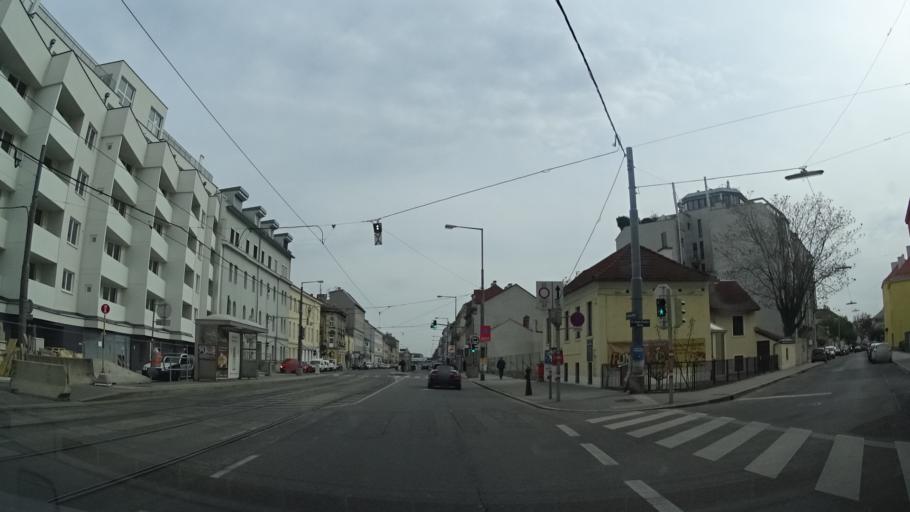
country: AT
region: Lower Austria
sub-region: Politischer Bezirk Korneuburg
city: Langenzersdorf
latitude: 48.2693
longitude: 16.3916
